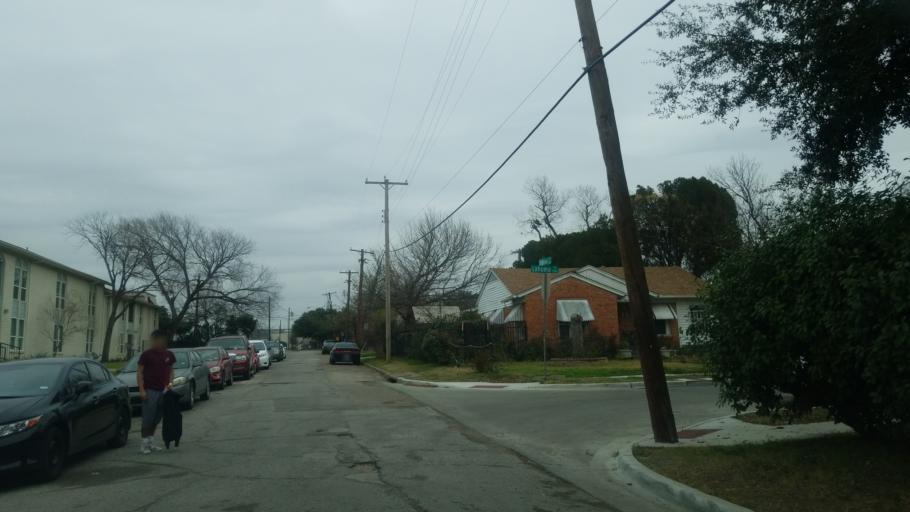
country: US
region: Texas
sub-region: Dallas County
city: Highland Park
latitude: 32.8230
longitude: -96.8238
